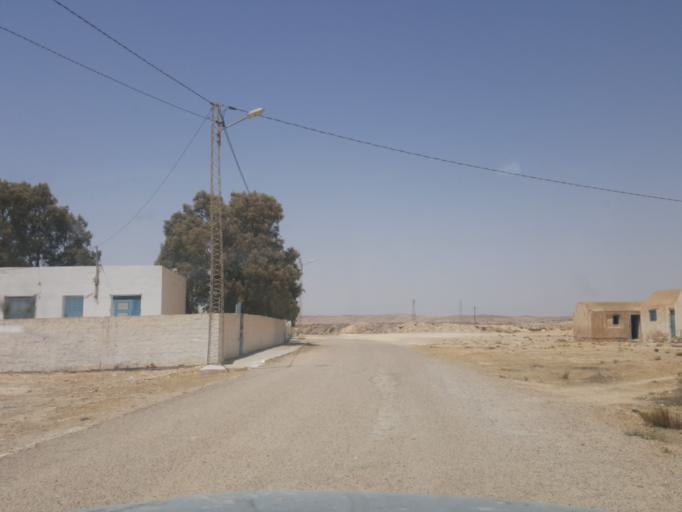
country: TN
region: Safaqis
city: Skhira
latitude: 34.1072
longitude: 9.9815
